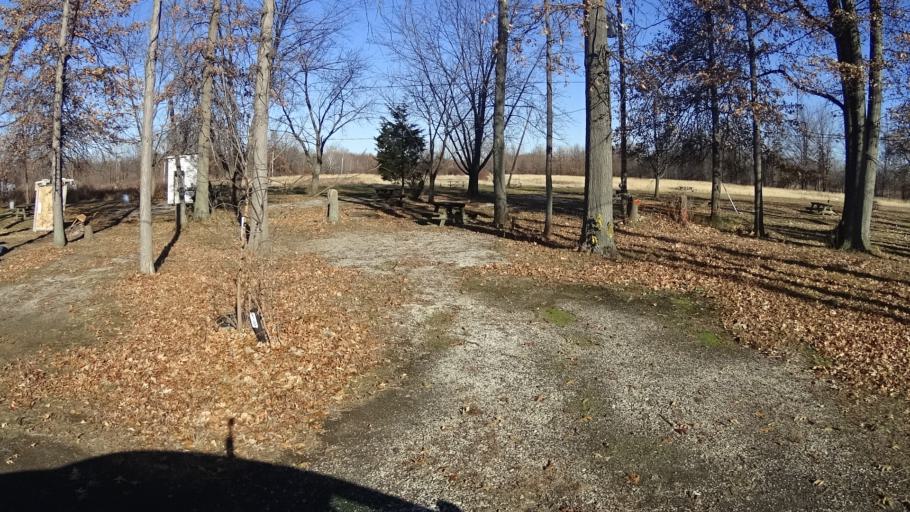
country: US
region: Ohio
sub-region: Lorain County
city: Avon
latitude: 41.4622
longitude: -82.0686
